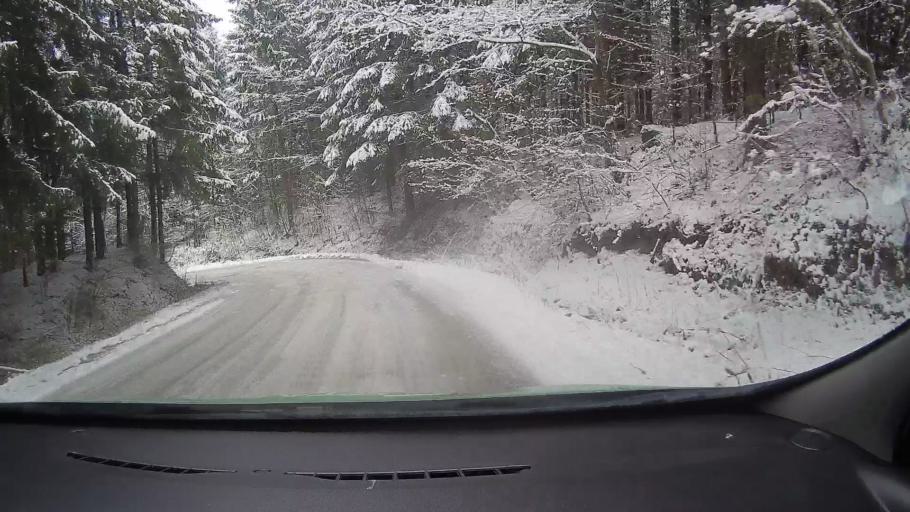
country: RO
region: Alba
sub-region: Comuna Almasu Mare
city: Almasu Mare
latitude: 46.0986
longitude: 23.1476
